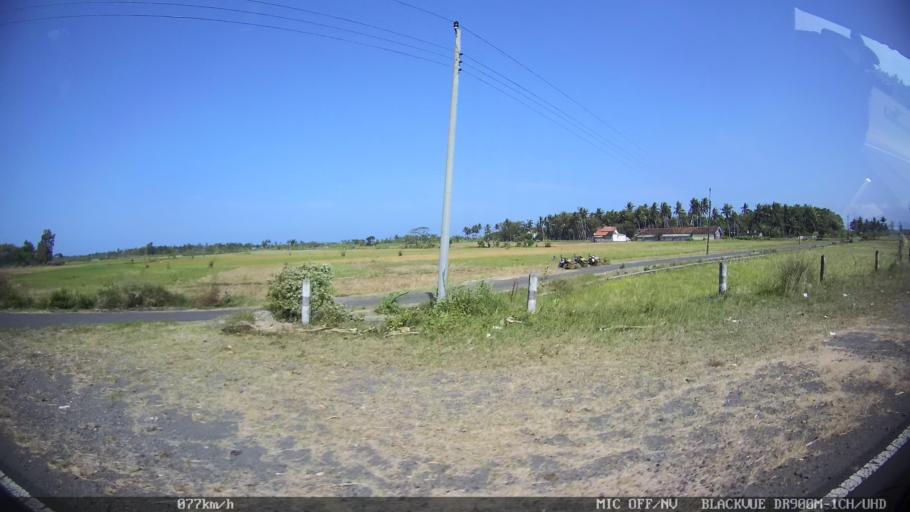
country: ID
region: Daerah Istimewa Yogyakarta
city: Srandakan
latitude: -7.9620
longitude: 110.2035
